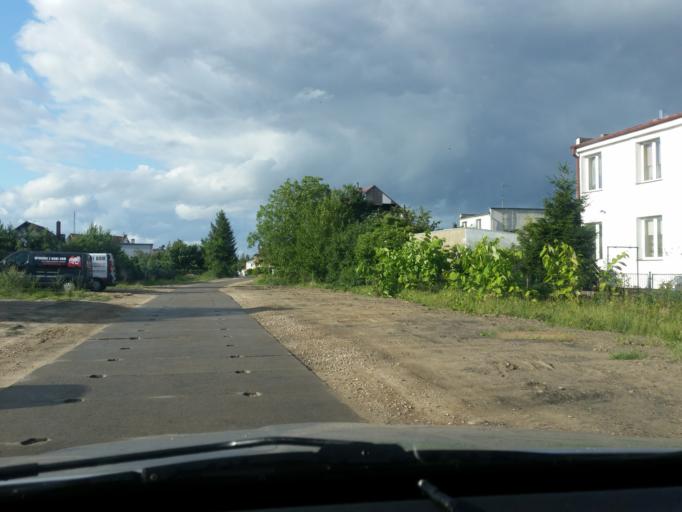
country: PL
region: Pomeranian Voivodeship
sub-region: Powiat chojnicki
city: Chojnice
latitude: 53.7030
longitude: 17.5448
